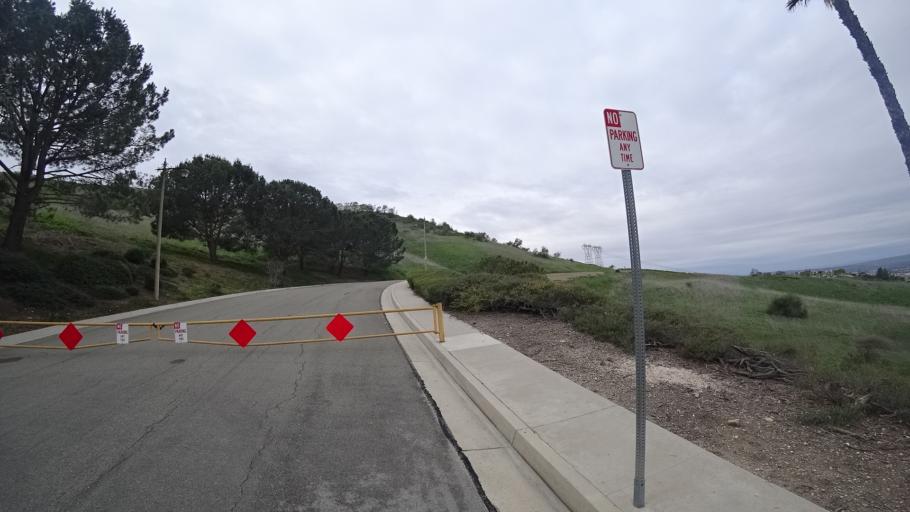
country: US
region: California
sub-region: Orange County
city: Villa Park
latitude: 33.8345
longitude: -117.7829
